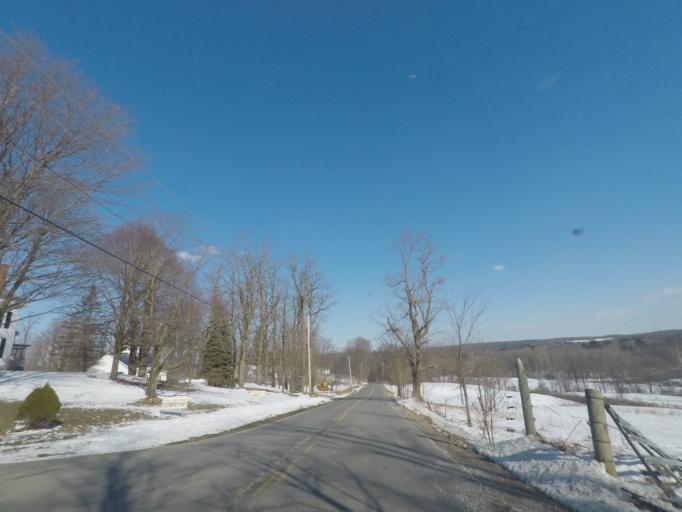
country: US
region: New York
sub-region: Saratoga County
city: Stillwater
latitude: 42.9218
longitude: -73.5310
